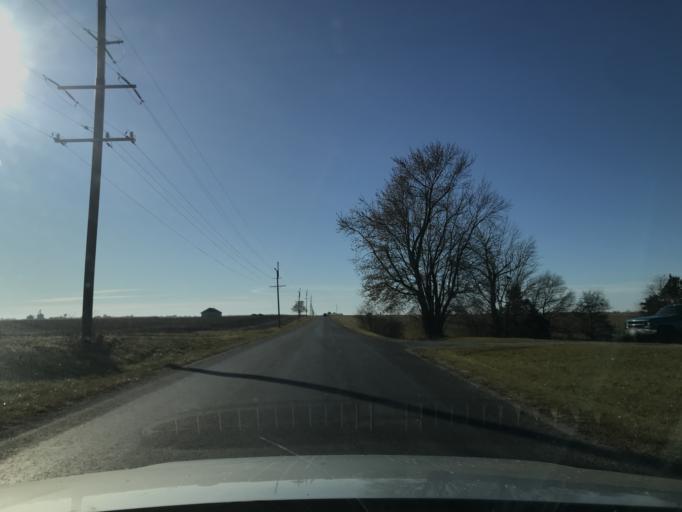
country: US
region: Illinois
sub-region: Hancock County
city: Carthage
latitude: 40.4869
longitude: -91.1780
